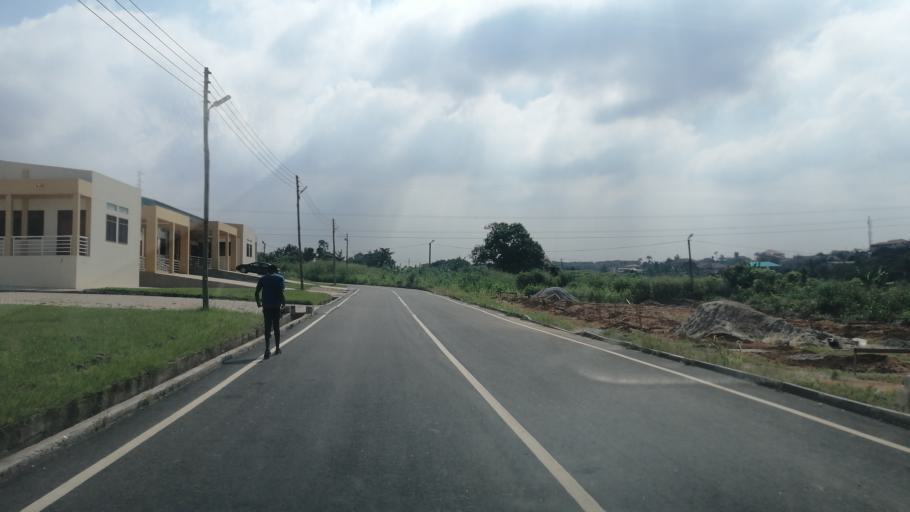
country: GH
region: Ashanti
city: Kumasi
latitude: 6.6999
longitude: -1.6789
